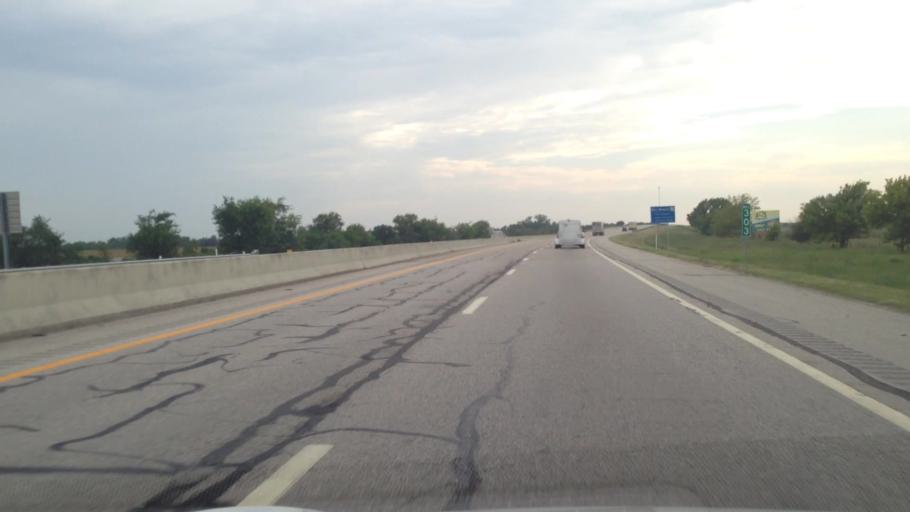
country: US
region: Oklahoma
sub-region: Ottawa County
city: Afton
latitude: 36.7284
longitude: -94.9205
